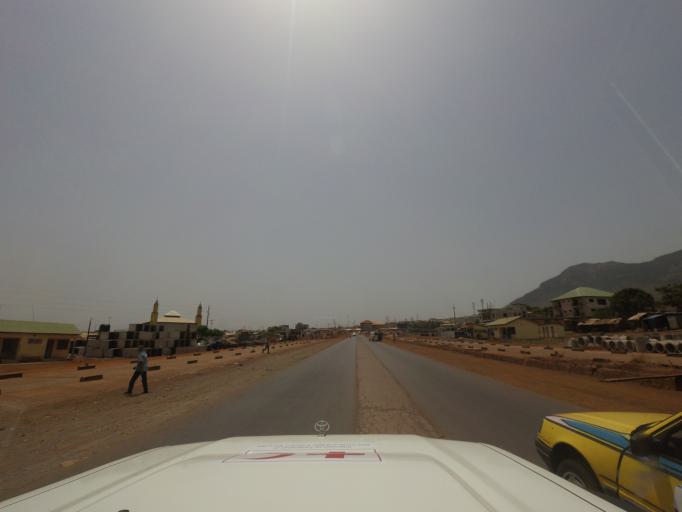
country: GN
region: Kindia
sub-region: Coyah
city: Coyah
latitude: 9.7309
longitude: -13.4306
